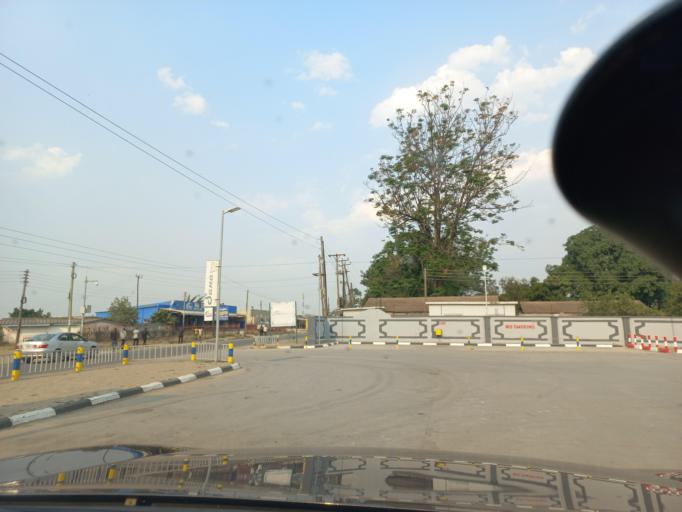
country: ZM
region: Lusaka
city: Lusaka
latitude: -15.4540
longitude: 28.2717
